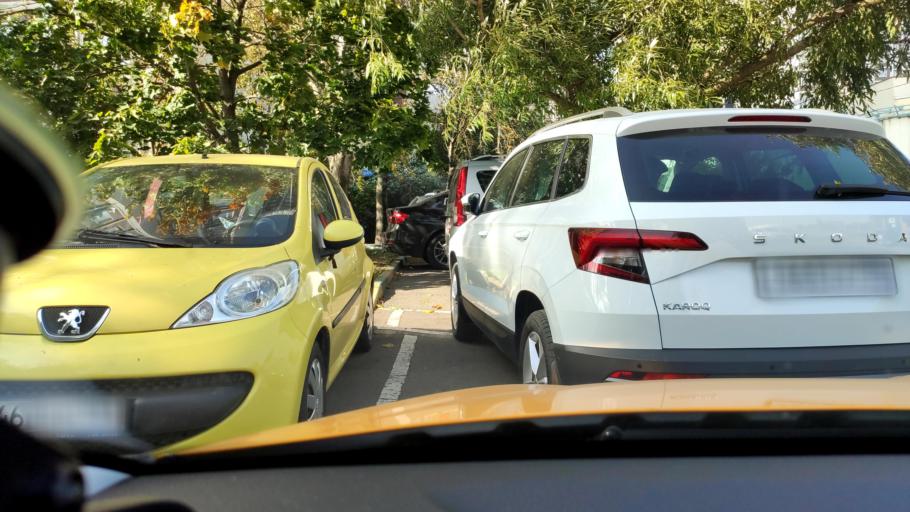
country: RU
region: Moscow
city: Strogino
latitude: 55.8002
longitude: 37.4121
